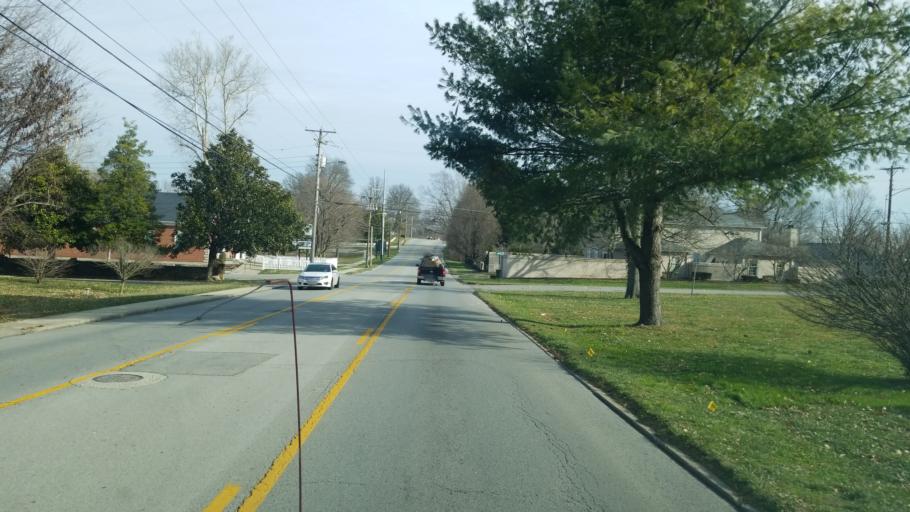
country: US
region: Kentucky
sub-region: Boyle County
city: Danville
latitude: 37.6497
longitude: -84.7623
